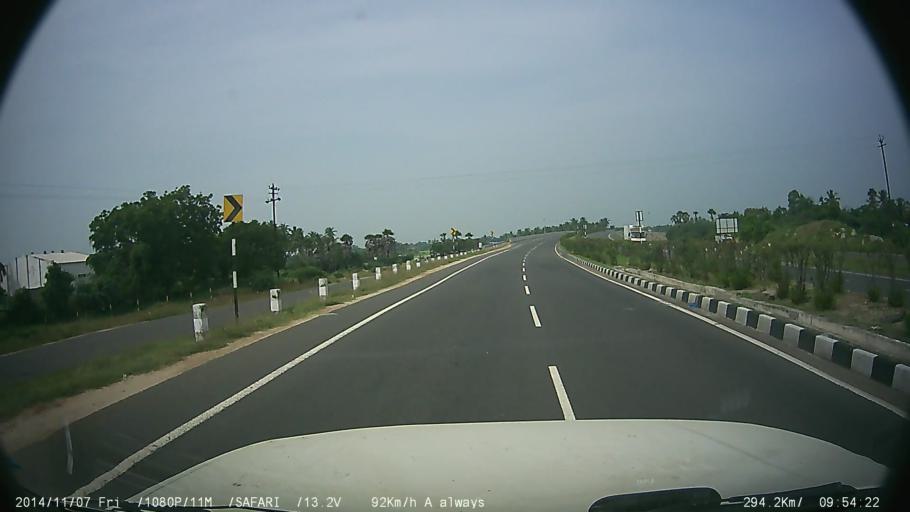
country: IN
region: Tamil Nadu
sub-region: Erode
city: Vijayapuri
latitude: 11.2368
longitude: 77.5048
